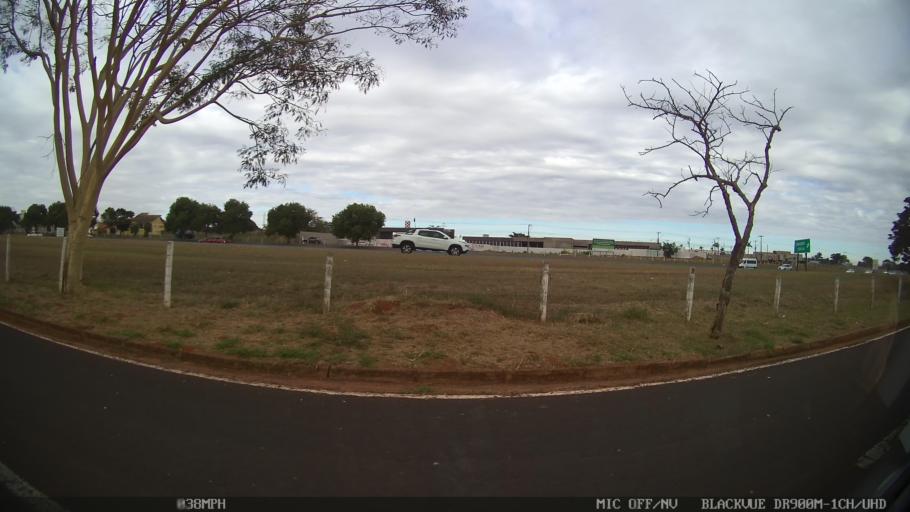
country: BR
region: Sao Paulo
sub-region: Sao Jose Do Rio Preto
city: Sao Jose do Rio Preto
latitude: -20.8232
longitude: -49.4146
